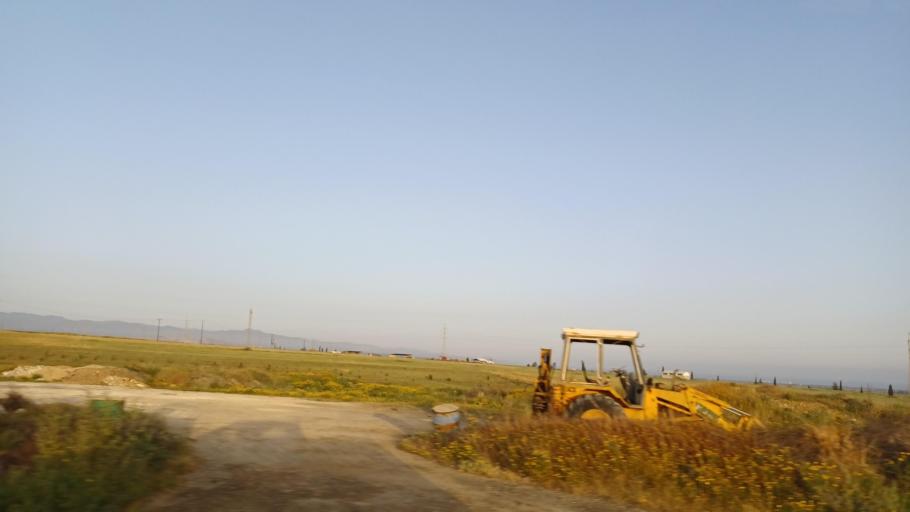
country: CY
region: Lefkosia
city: Astromeritis
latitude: 35.1162
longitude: 33.0149
